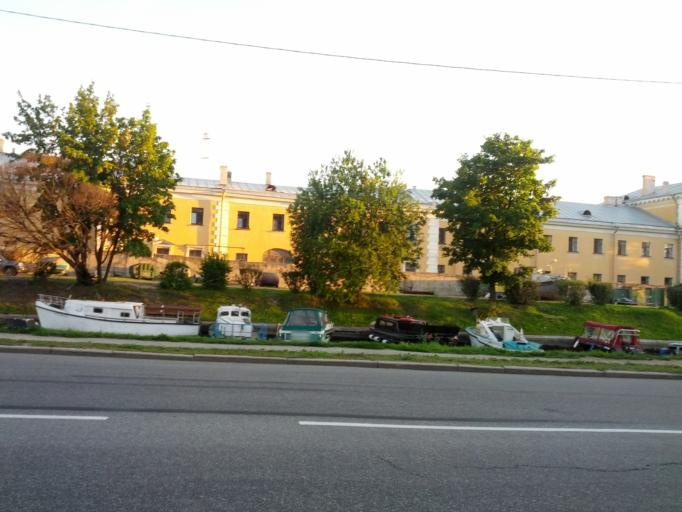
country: RU
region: St.-Petersburg
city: Petrogradka
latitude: 59.9680
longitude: 30.3300
